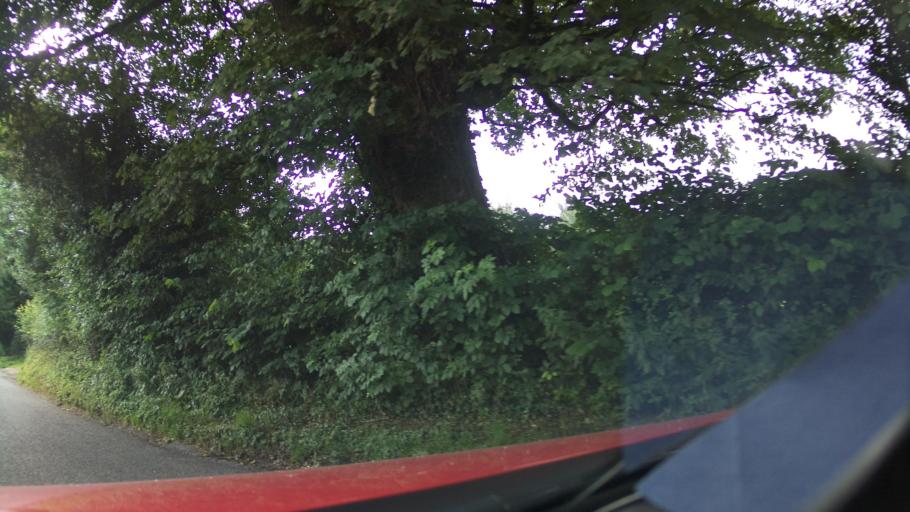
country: GB
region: England
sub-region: Bath and North East Somerset
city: Cameley
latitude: 51.2608
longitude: -2.5628
